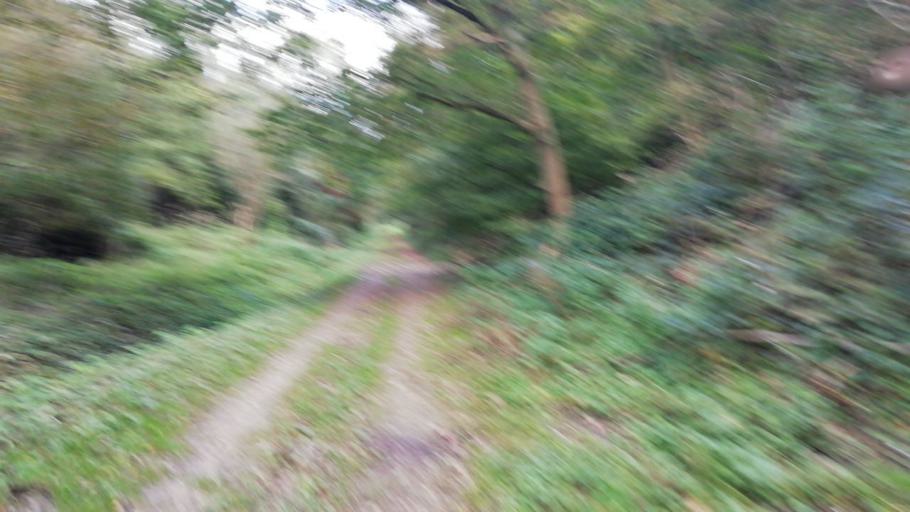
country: FR
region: Haute-Normandie
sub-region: Departement de la Seine-Maritime
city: Rogerville
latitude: 49.5016
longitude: 0.2506
